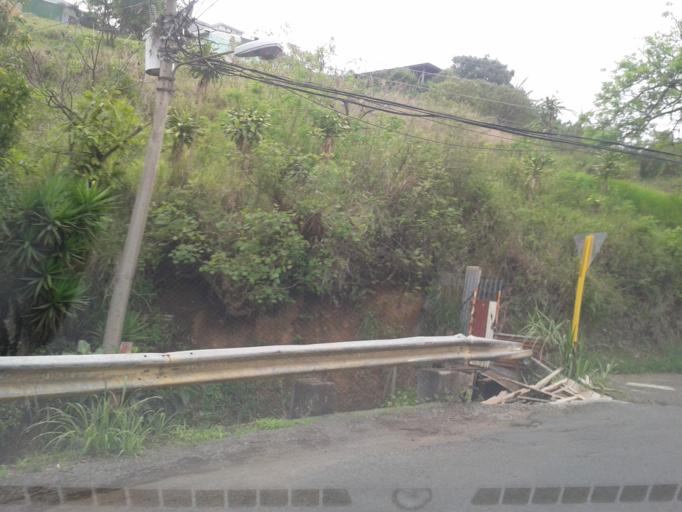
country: CR
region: Heredia
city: San Pablo
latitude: 9.9808
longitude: -84.1003
